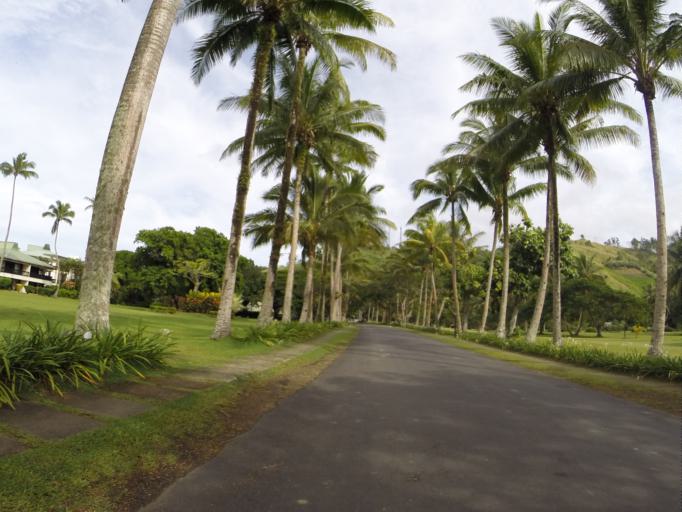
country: FJ
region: Western
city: Nadi
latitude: -18.2014
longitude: 177.6942
